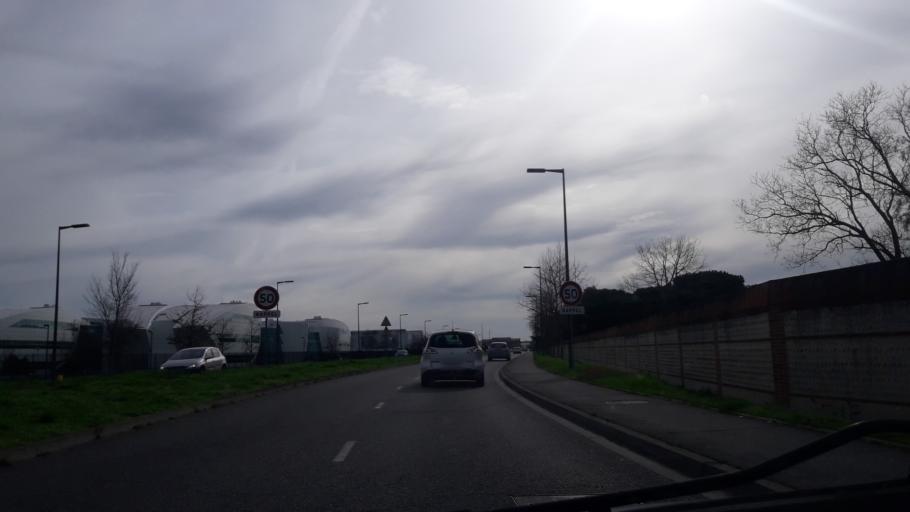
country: FR
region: Midi-Pyrenees
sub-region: Departement de la Haute-Garonne
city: Vieille-Toulouse
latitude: 43.5626
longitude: 1.4251
